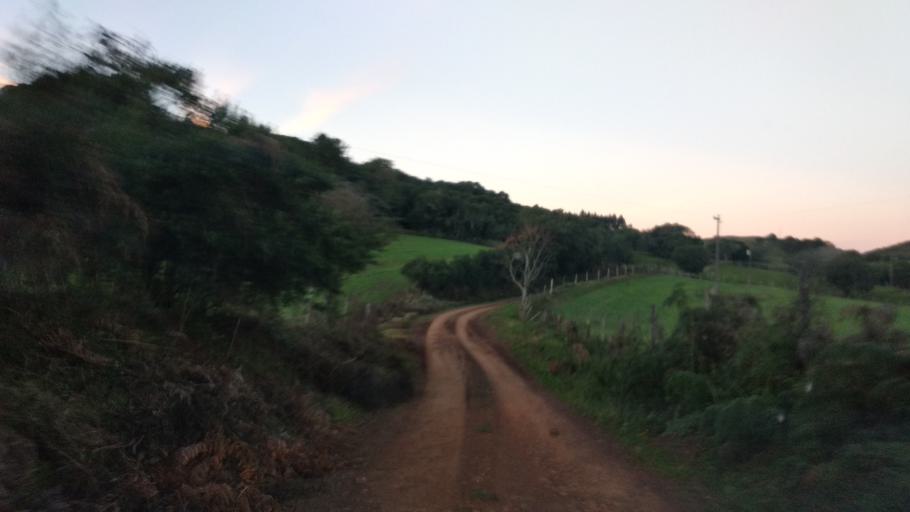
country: BR
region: Santa Catarina
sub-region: Celso Ramos
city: Celso Ramos
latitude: -27.5585
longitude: -51.2272
